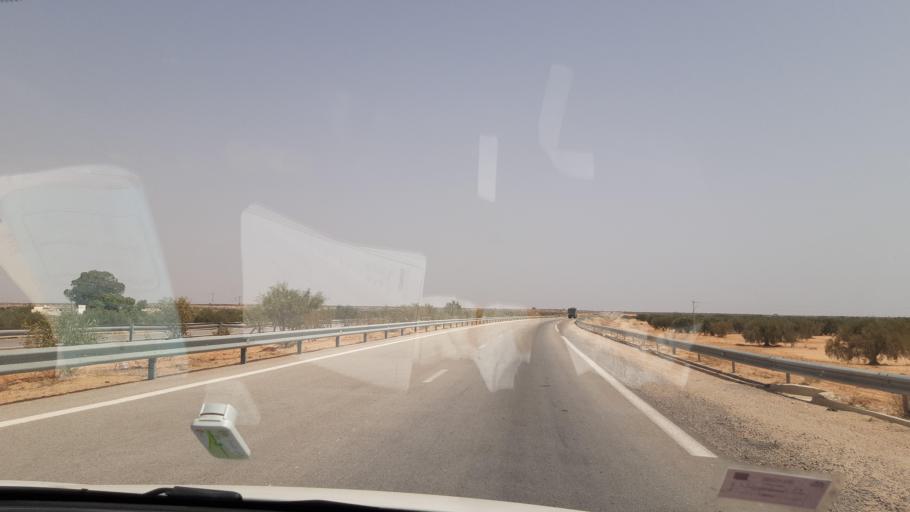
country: TN
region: Safaqis
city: Bi'r `Ali Bin Khalifah
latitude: 34.5260
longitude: 10.1317
